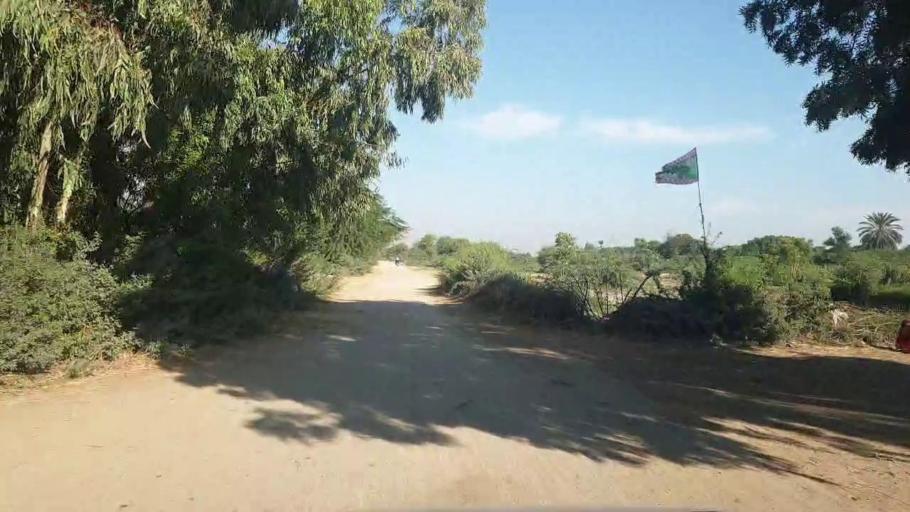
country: PK
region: Sindh
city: Talhar
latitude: 24.9389
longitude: 68.7895
